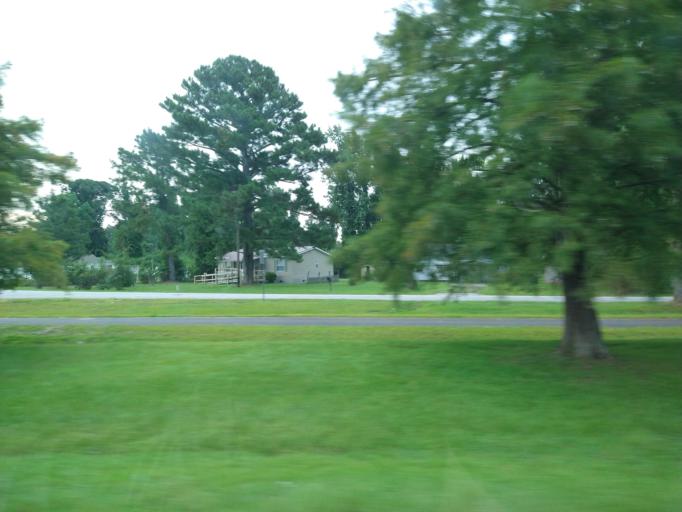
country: US
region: North Carolina
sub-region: Onslow County
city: Jacksonville
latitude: 34.7699
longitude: -77.4027
